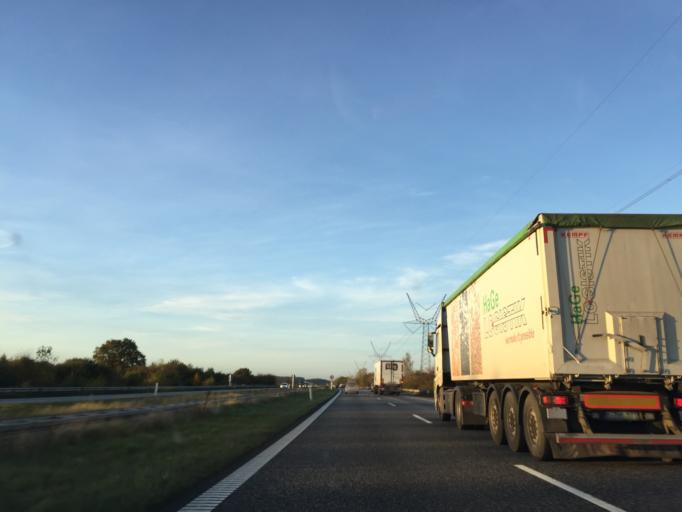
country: DK
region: South Denmark
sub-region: Kolding Kommune
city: Kolding
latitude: 55.4364
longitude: 9.4588
